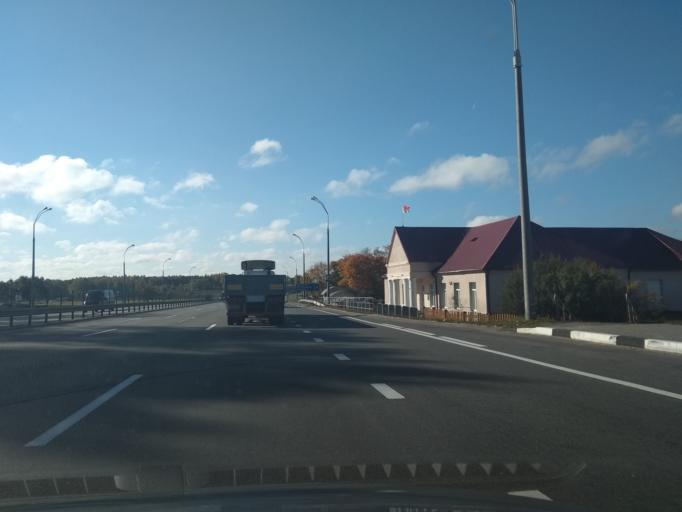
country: BY
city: Fanipol
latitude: 53.7389
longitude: 27.3087
